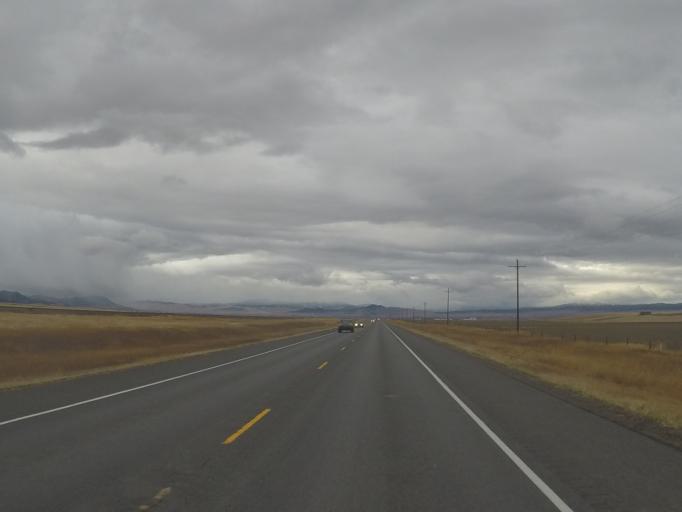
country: US
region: Montana
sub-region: Lewis and Clark County
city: East Helena
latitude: 46.5761
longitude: -111.8357
